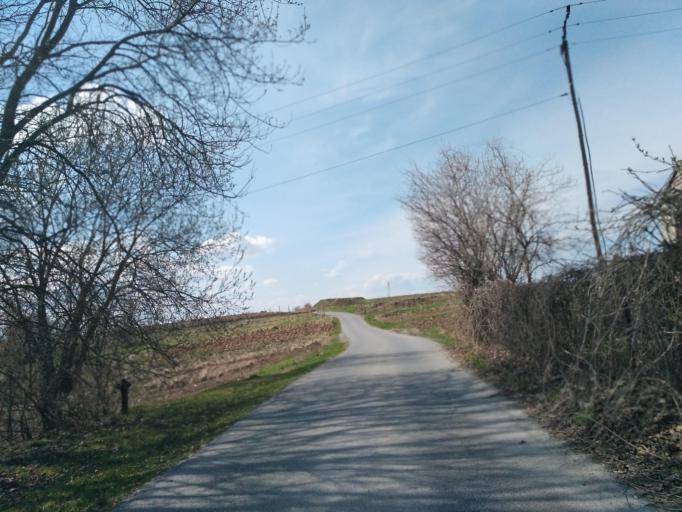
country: PL
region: Subcarpathian Voivodeship
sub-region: Powiat ropczycko-sedziszowski
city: Sedziszow Malopolski
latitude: 50.0455
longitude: 21.7126
